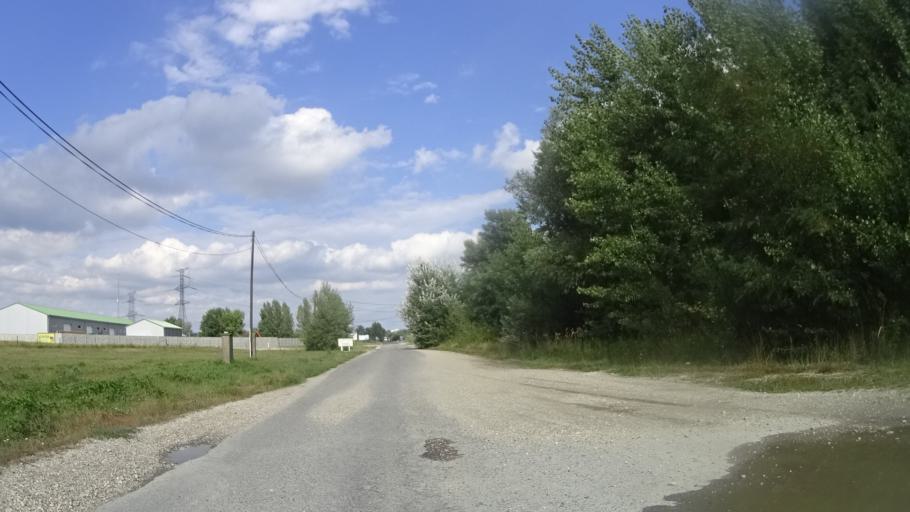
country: SK
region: Trnavsky
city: Gabcikovo
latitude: 47.8825
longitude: 17.5485
